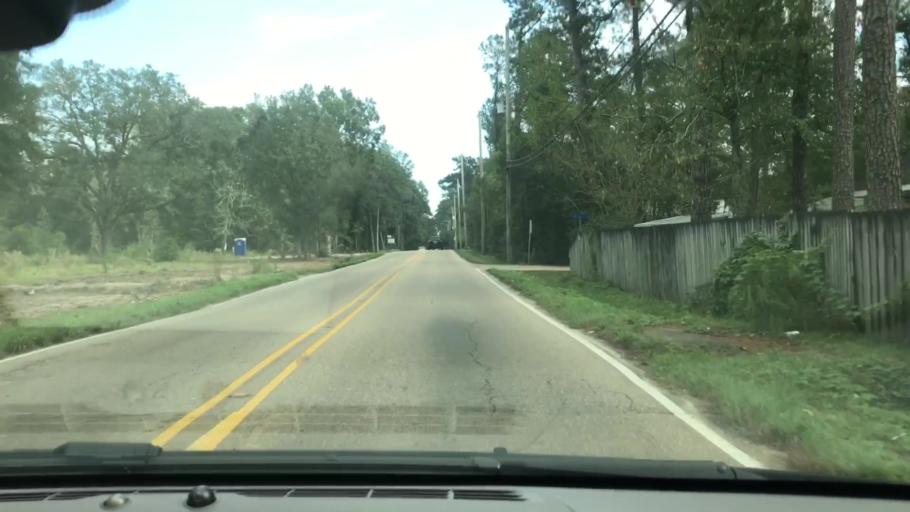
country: US
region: Louisiana
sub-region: Saint Tammany Parish
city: Covington
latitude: 30.4598
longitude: -90.0743
